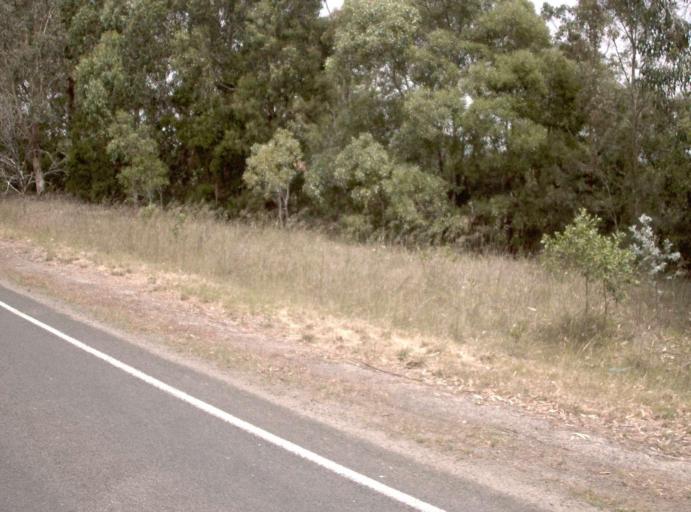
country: AU
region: Victoria
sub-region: Latrobe
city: Traralgon
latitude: -38.4916
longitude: 146.7131
